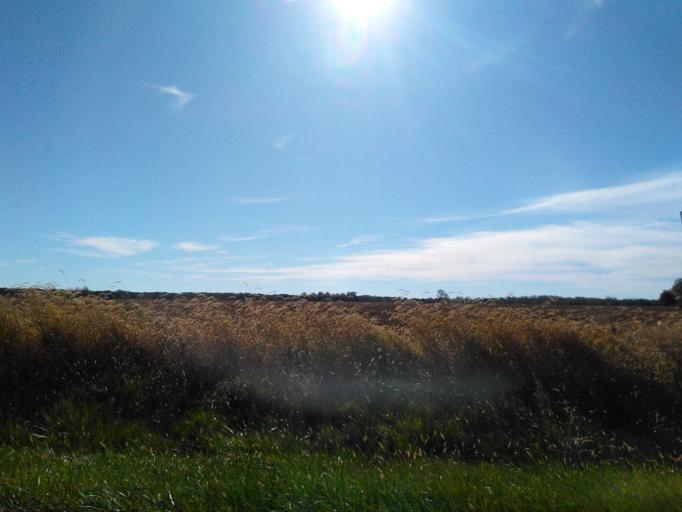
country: US
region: Illinois
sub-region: Madison County
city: Highland
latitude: 38.7788
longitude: -89.6339
